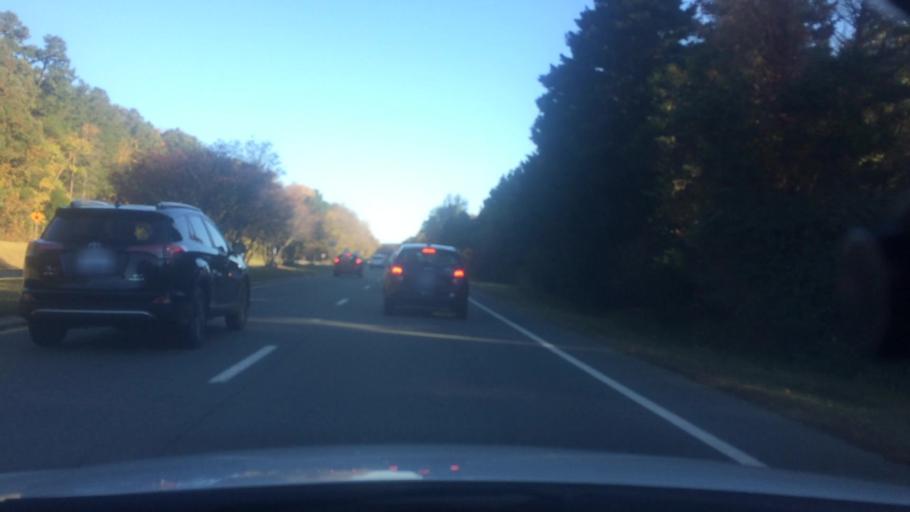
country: US
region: North Carolina
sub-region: Orange County
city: Chapel Hill
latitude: 35.9190
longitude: -79.0260
